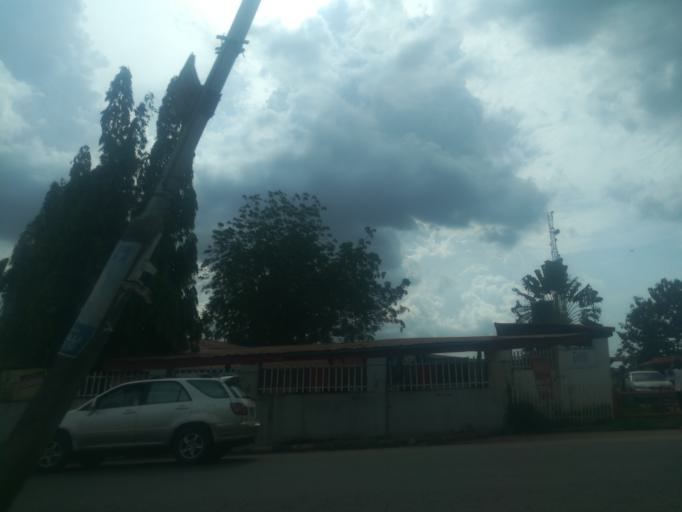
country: NG
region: Oyo
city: Ibadan
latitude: 7.4377
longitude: 3.9093
